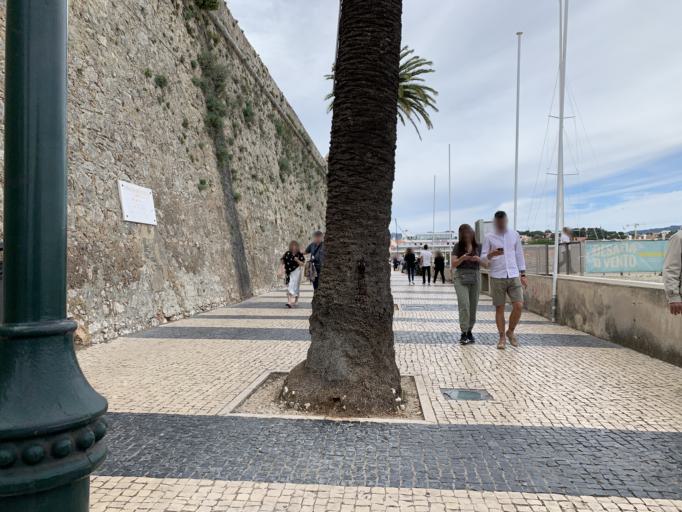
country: PT
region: Lisbon
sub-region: Cascais
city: Cascais
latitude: 38.6947
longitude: -9.4188
